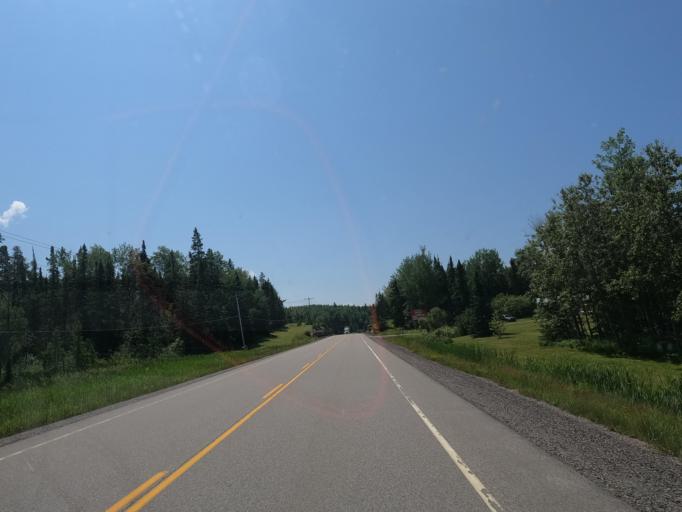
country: CA
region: Ontario
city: Dryden
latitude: 49.8679
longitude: -93.3593
